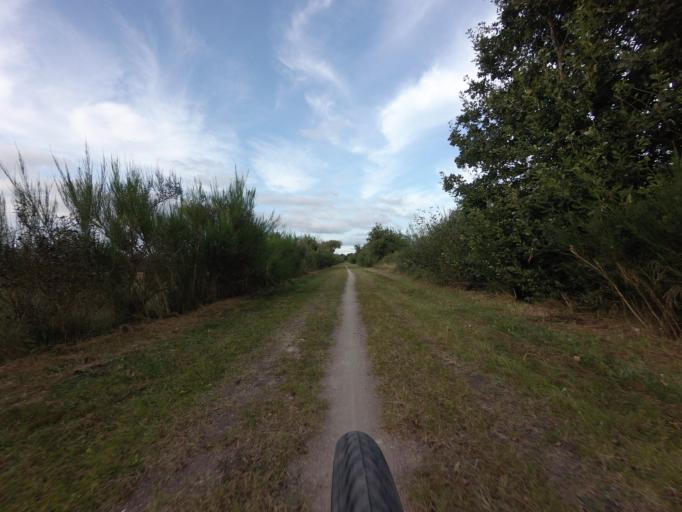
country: DK
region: Central Jutland
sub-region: Ikast-Brande Kommune
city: Brande
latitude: 55.8991
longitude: 9.0747
